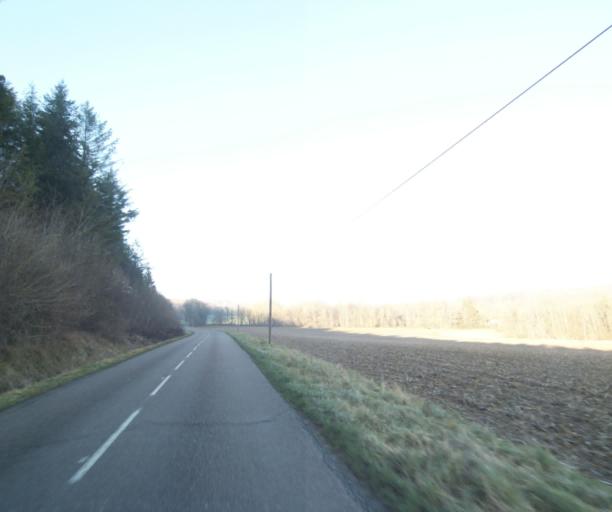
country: FR
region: Champagne-Ardenne
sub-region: Departement de la Haute-Marne
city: Bienville
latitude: 48.5614
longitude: 5.0826
